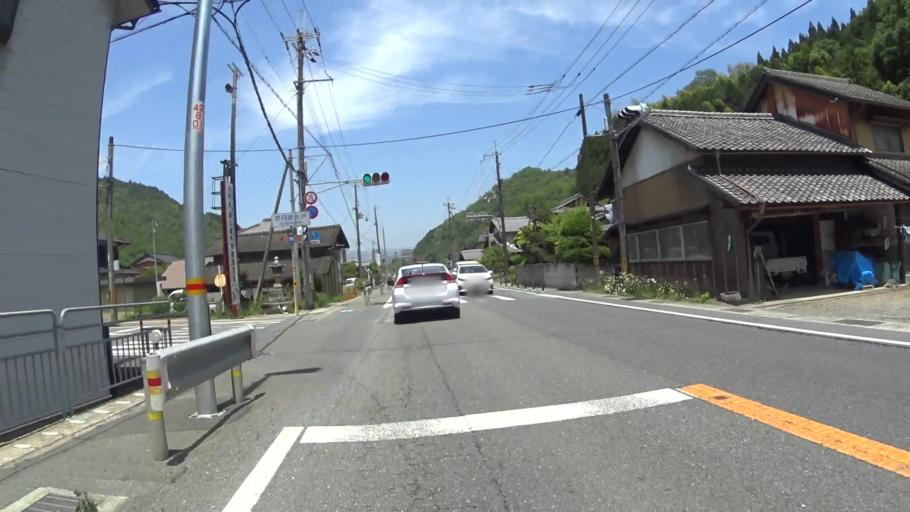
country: JP
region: Kyoto
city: Kameoka
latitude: 35.1393
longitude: 135.4254
